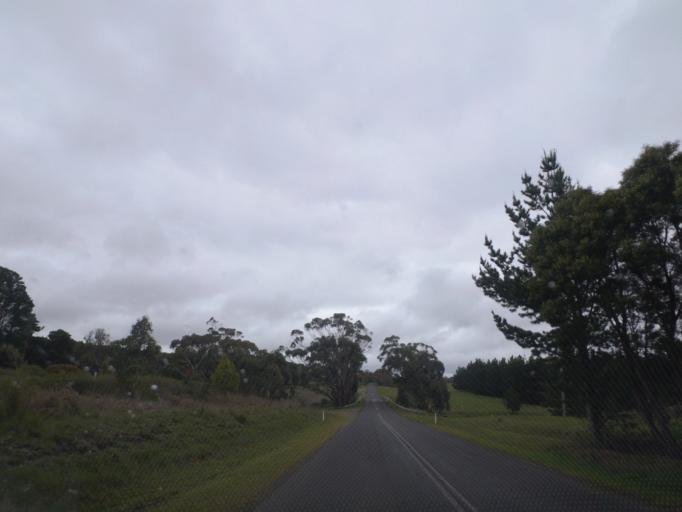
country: AU
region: Victoria
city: Brown Hill
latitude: -37.5946
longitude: 144.1656
